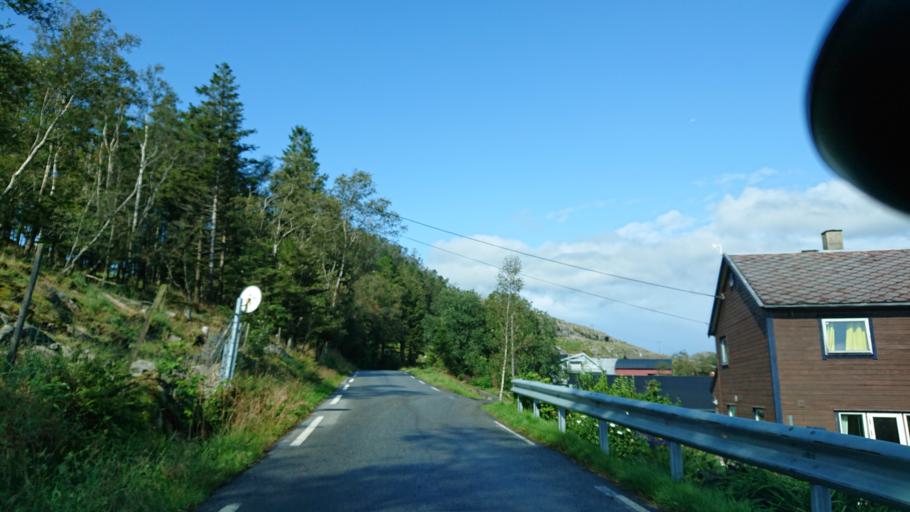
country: NO
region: Rogaland
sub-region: Gjesdal
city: Algard
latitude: 58.6942
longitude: 5.8829
